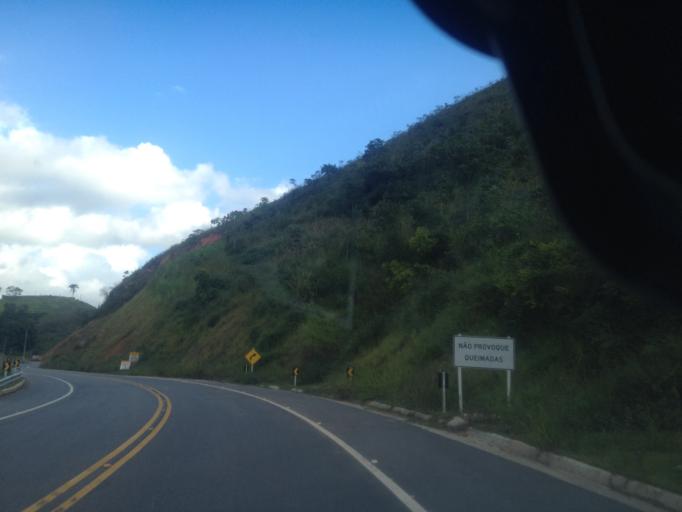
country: BR
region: Rio de Janeiro
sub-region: Quatis
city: Quatis
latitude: -22.2792
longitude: -44.2588
